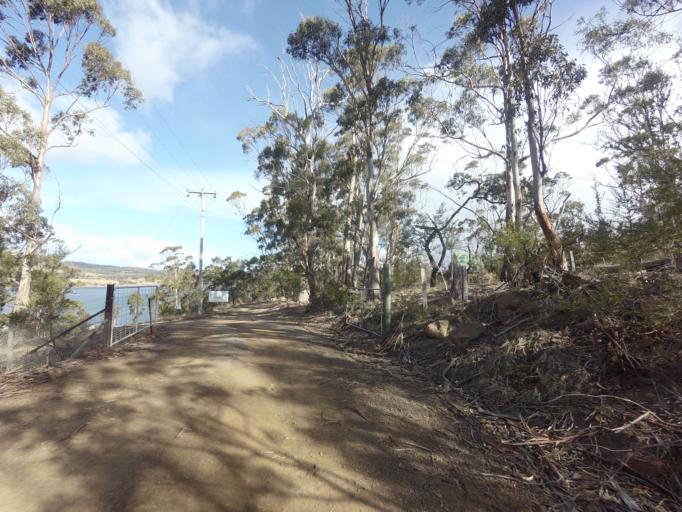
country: AU
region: Tasmania
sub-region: Sorell
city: Sorell
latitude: -42.3314
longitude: 147.9673
